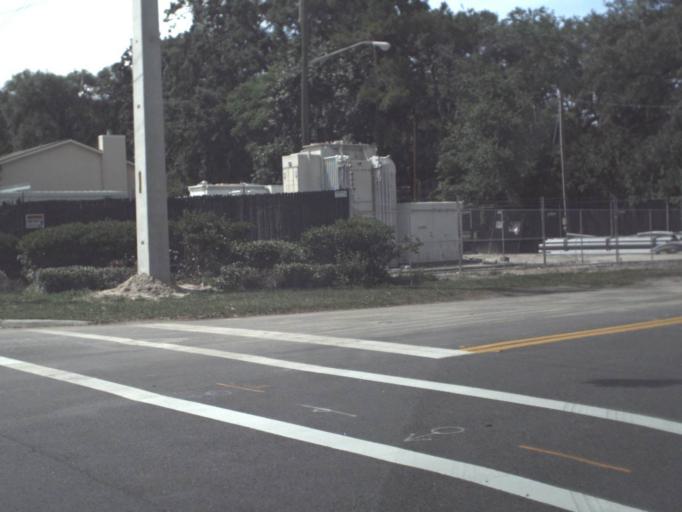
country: US
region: Florida
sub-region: Duval County
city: Jacksonville
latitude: 30.2661
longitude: -81.7078
